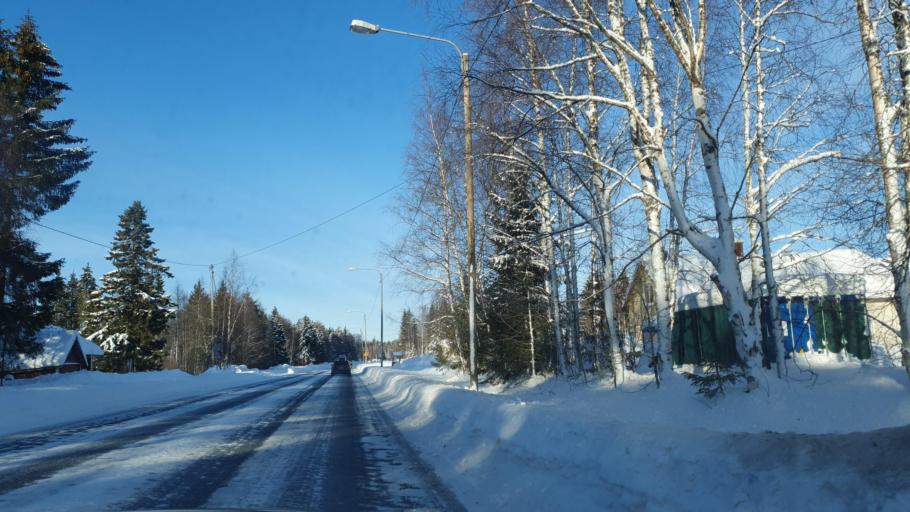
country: FI
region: Lapland
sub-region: Kemi-Tornio
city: Tornio
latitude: 65.9561
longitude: 24.0590
